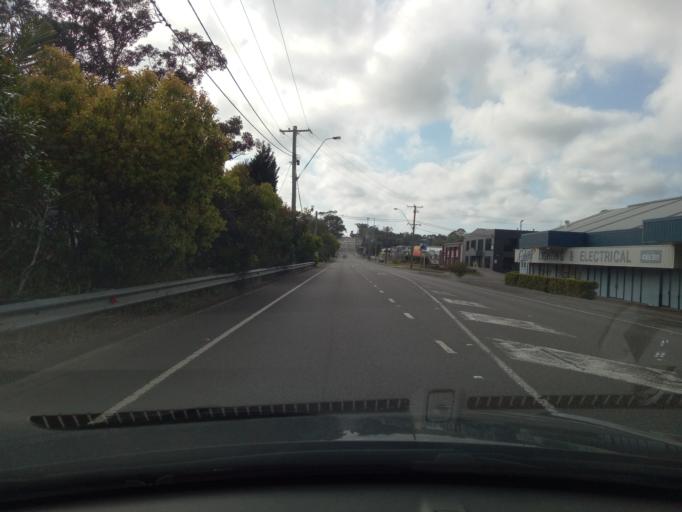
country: AU
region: New South Wales
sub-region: Gosford Shire
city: Erina
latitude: -33.4329
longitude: 151.3838
